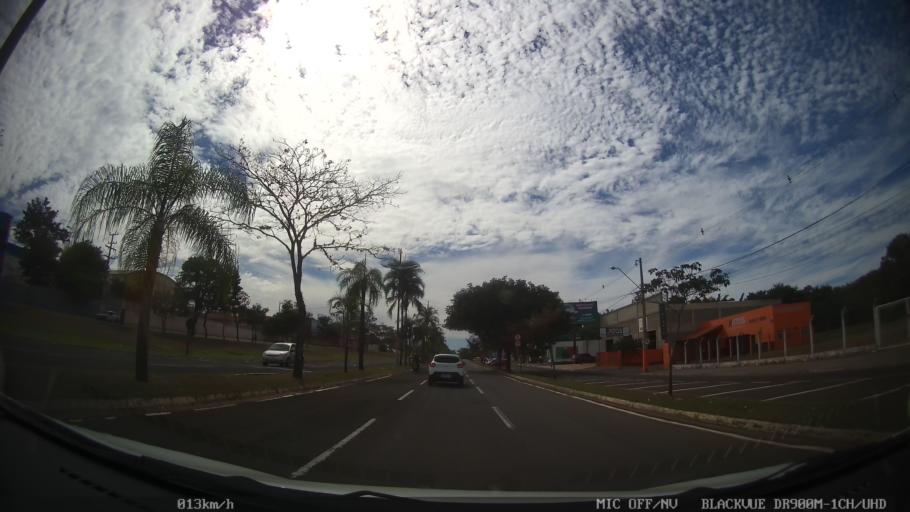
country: BR
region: Sao Paulo
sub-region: Catanduva
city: Catanduva
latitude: -21.1555
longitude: -48.9832
